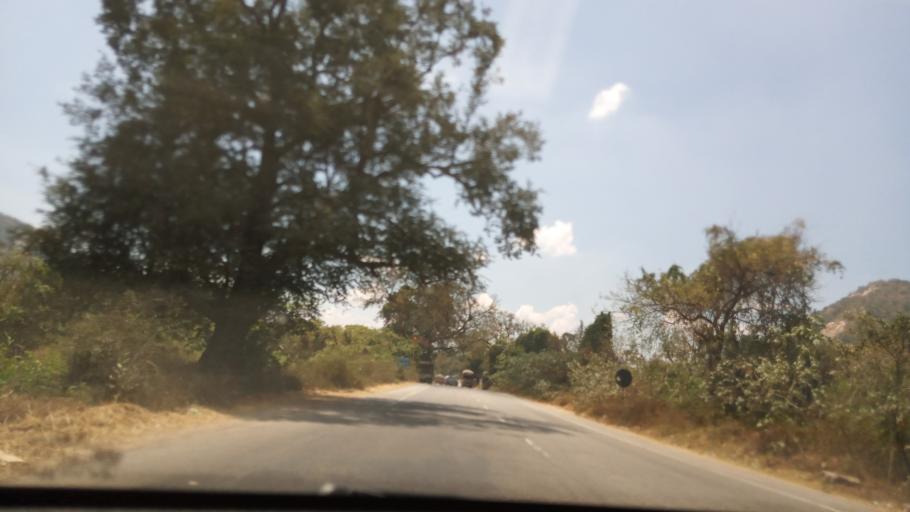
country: IN
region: Andhra Pradesh
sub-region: Chittoor
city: Narasingapuram
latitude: 13.5333
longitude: 79.2264
